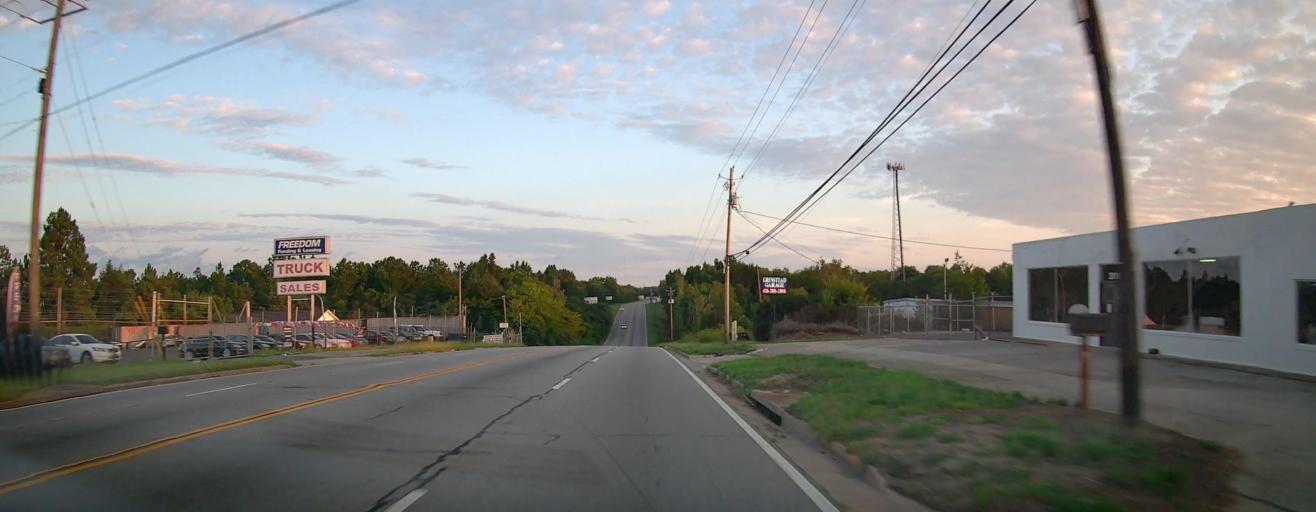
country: US
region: Georgia
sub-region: Bibb County
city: Macon
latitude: 32.8051
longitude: -83.6405
